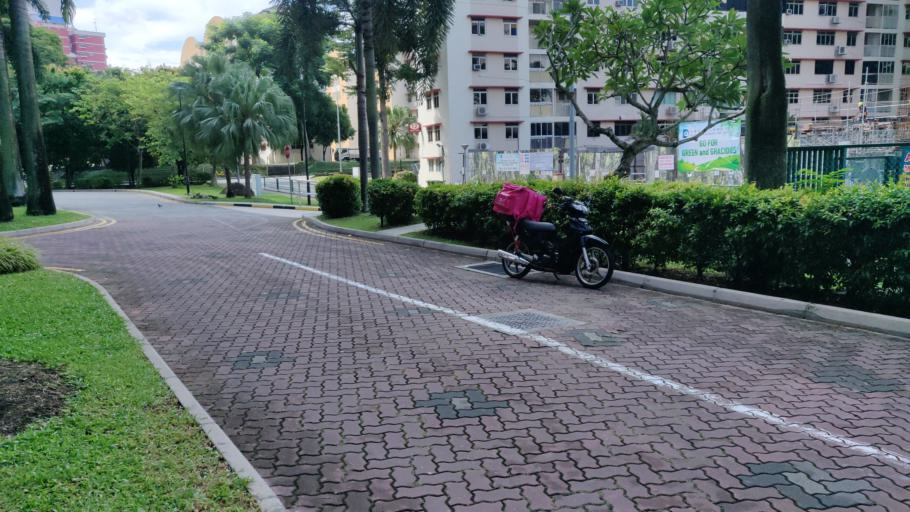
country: SG
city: Singapore
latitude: 1.2867
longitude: 103.8162
